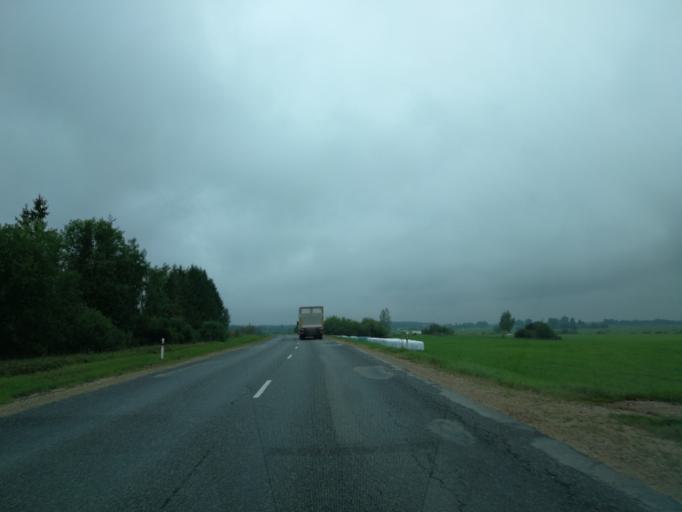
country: LV
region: Livani
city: Livani
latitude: 56.3541
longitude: 26.2435
